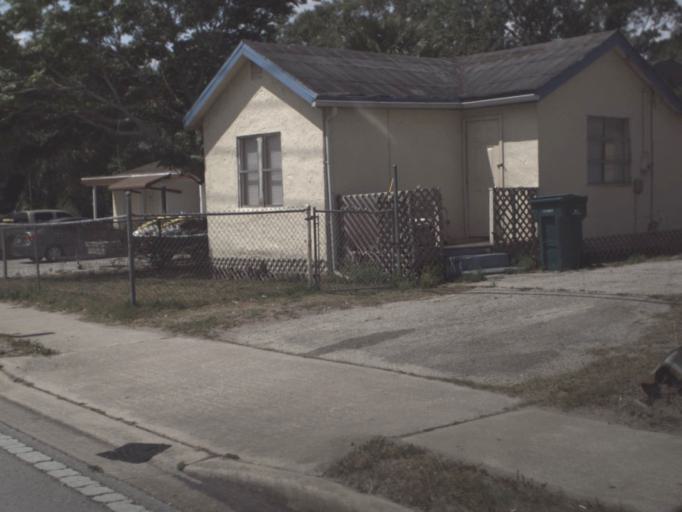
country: US
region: Florida
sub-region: Brevard County
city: Cocoa West
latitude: 28.3619
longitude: -80.7551
